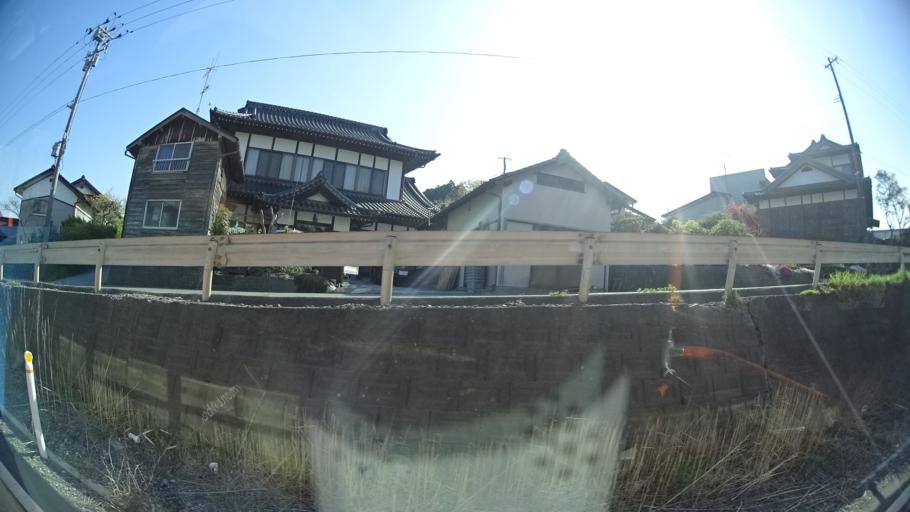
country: JP
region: Iwate
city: Ofunato
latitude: 39.0129
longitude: 141.7163
